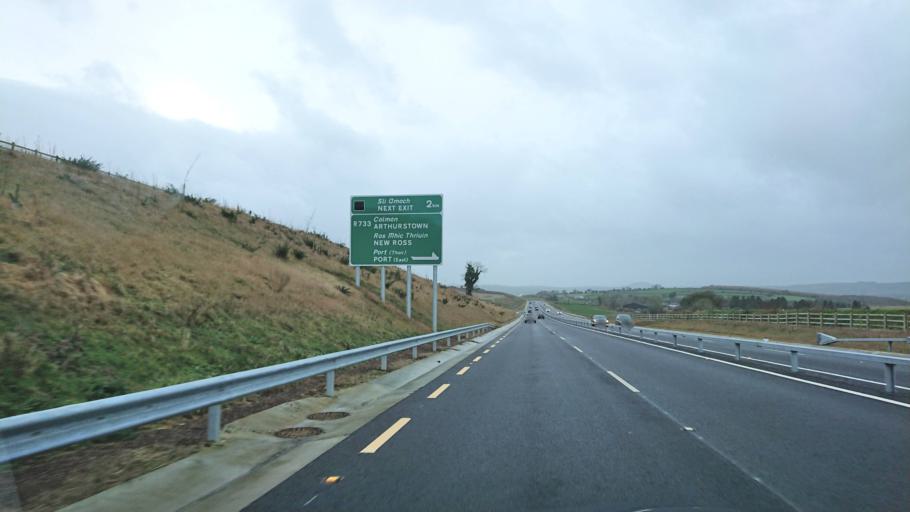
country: IE
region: Leinster
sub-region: Loch Garman
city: New Ross
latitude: 52.3714
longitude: -6.9310
